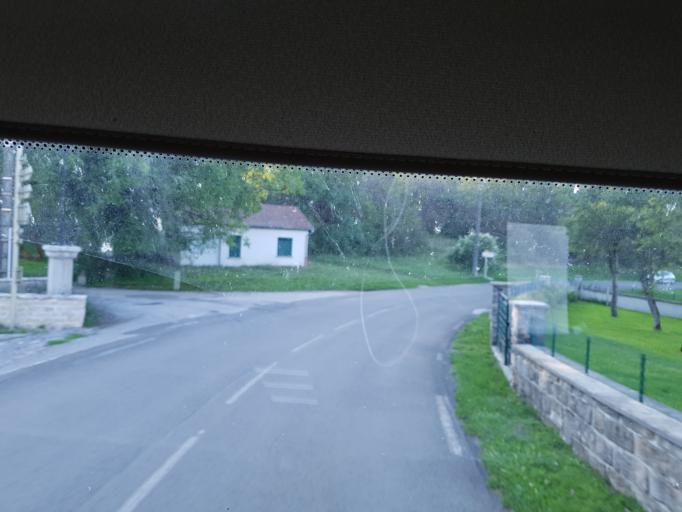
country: FR
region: Franche-Comte
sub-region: Departement du Jura
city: Moirans-en-Montagne
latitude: 46.4035
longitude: 5.6490
